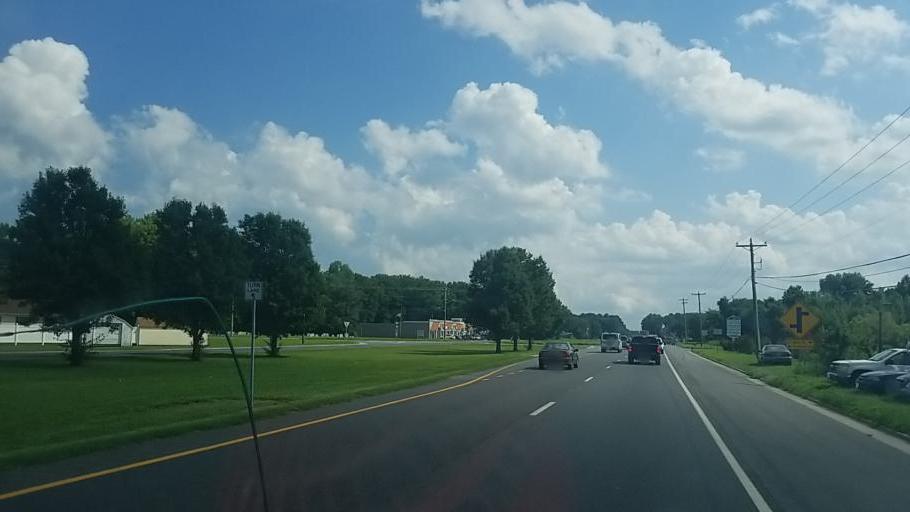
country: US
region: Delaware
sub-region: Sussex County
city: Selbyville
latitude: 38.5139
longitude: -75.2387
